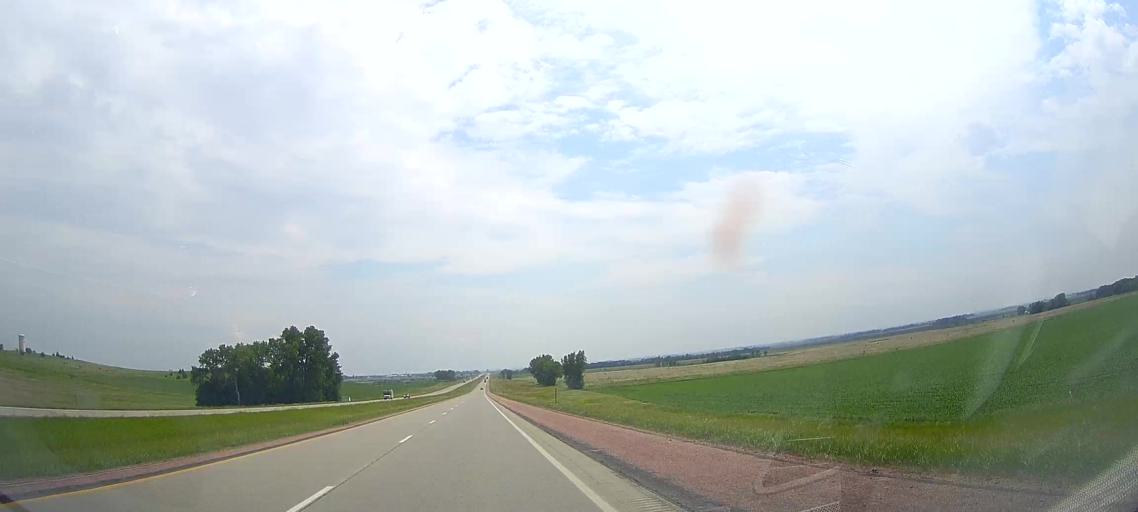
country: US
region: South Dakota
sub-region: Clay County
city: Vermillion
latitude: 42.8980
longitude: -96.7954
